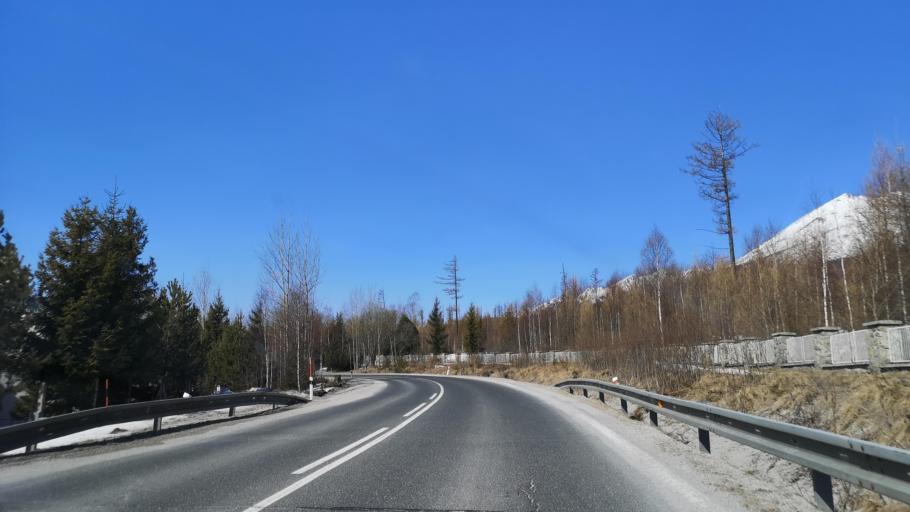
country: SK
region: Presovsky
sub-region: Okres Poprad
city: Svit
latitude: 49.1187
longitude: 20.1503
